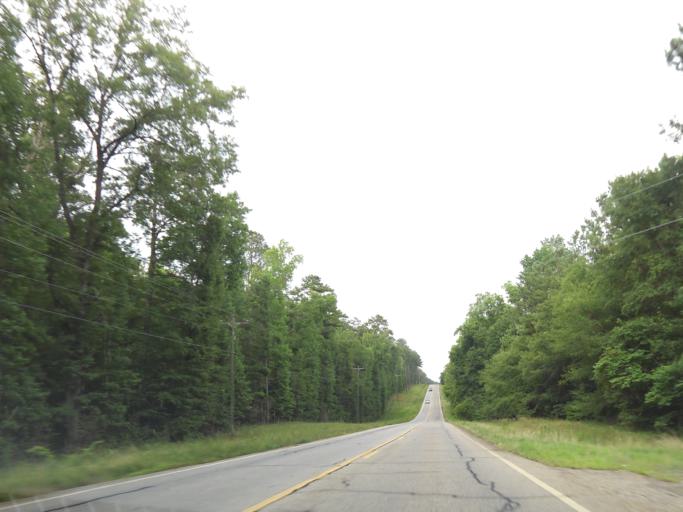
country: US
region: Georgia
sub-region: Bibb County
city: West Point
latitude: 32.8656
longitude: -83.8269
